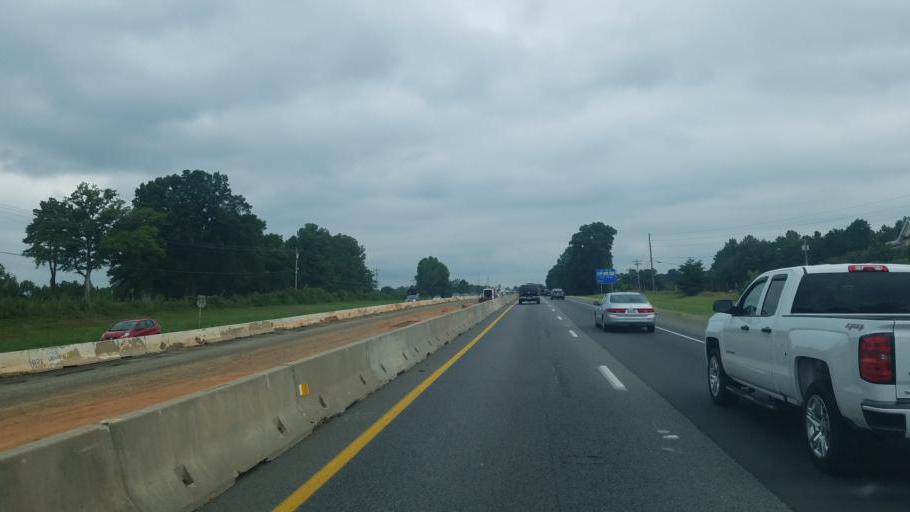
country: US
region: North Carolina
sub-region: Mecklenburg County
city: Cornelius
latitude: 35.4748
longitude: -80.8747
